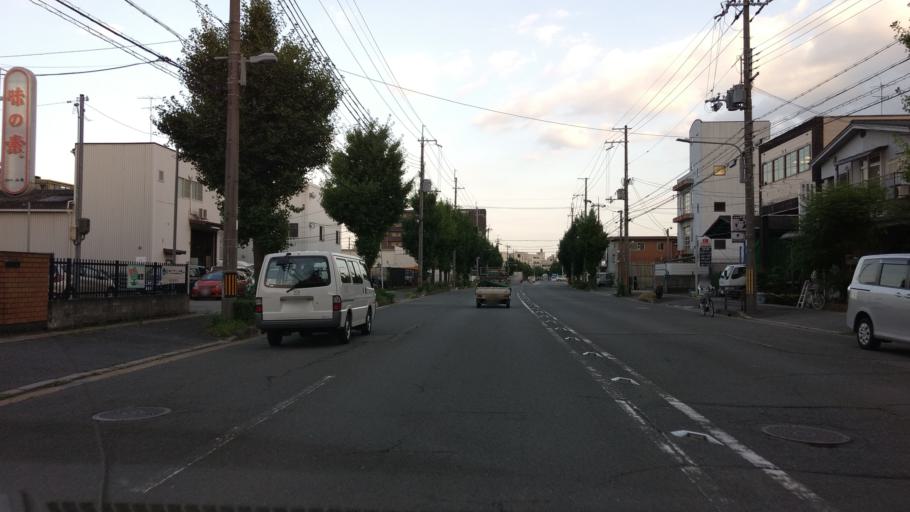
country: JP
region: Kyoto
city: Muko
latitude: 34.9612
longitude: 135.7285
